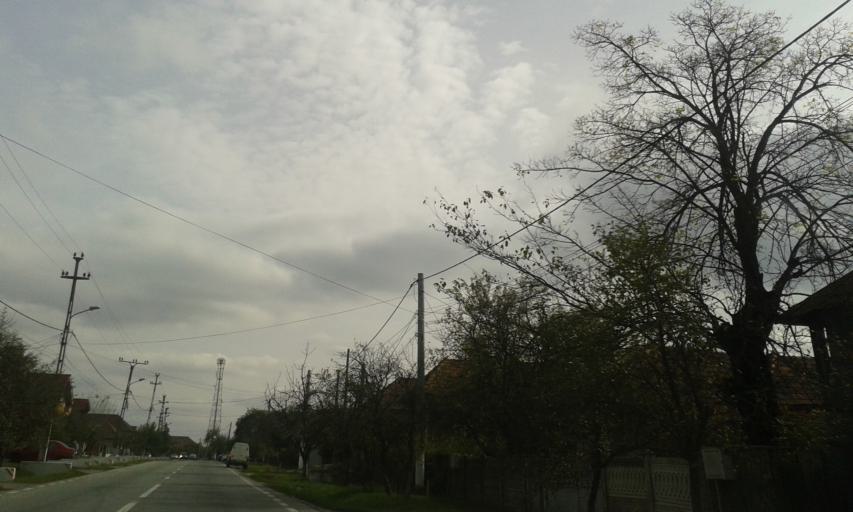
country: RO
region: Gorj
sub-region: Comuna Balanesti
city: Balanesti
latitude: 45.0424
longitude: 23.3484
